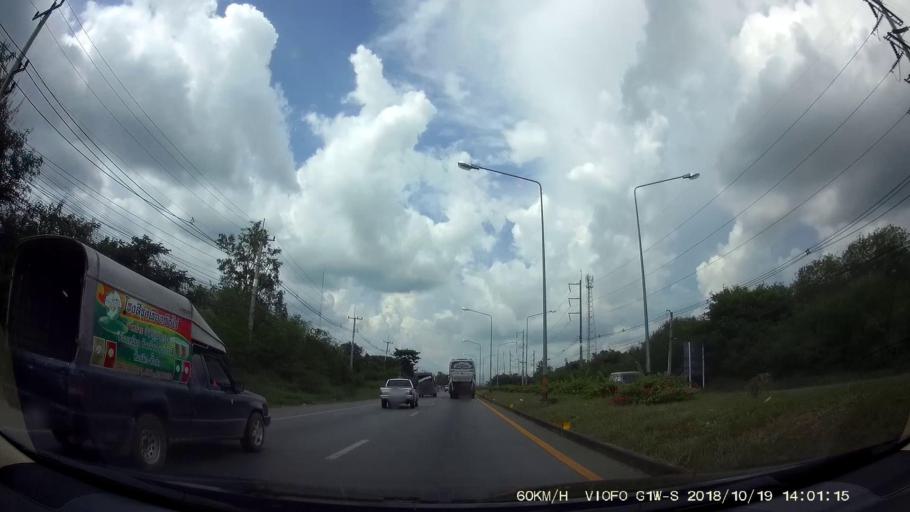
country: TH
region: Chaiyaphum
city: Chaiyaphum
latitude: 15.8274
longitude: 102.0589
